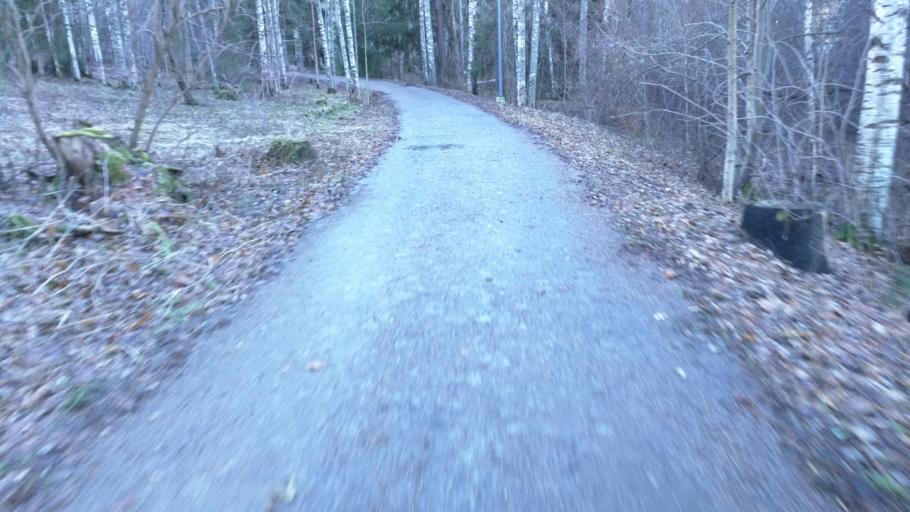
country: FI
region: Uusimaa
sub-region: Helsinki
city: Kauniainen
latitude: 60.2371
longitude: 24.7160
